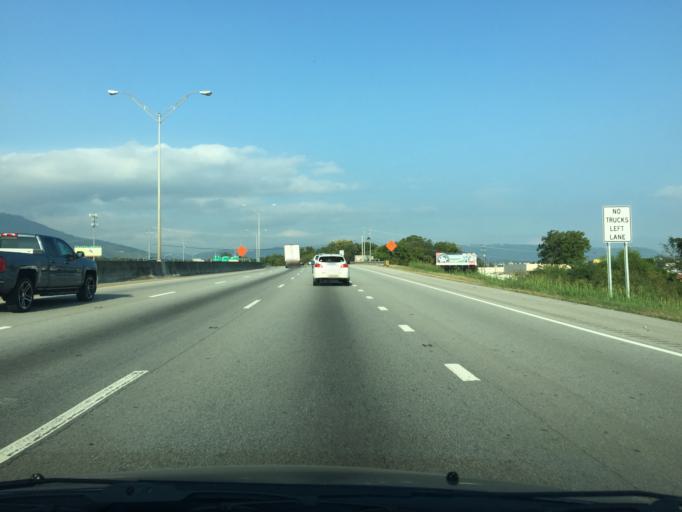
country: US
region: Tennessee
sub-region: Hamilton County
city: East Ridge
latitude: 35.0181
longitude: -85.2856
